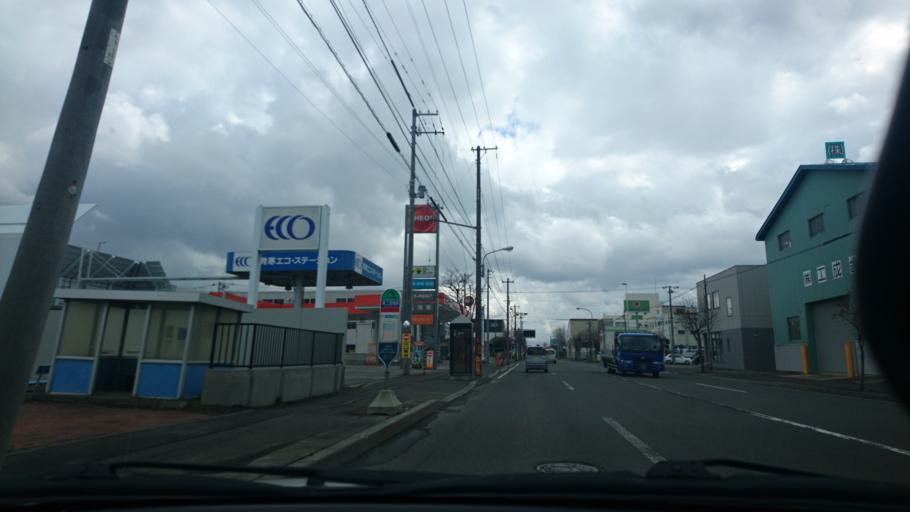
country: JP
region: Hokkaido
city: Sapporo
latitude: 43.1047
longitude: 141.2857
